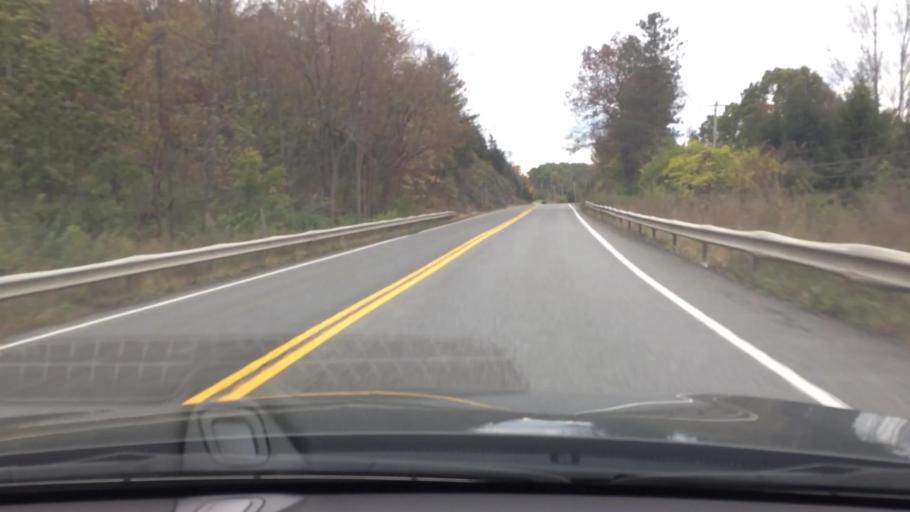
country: US
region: New York
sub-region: Columbia County
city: Kinderhook
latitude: 42.3880
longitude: -73.6885
